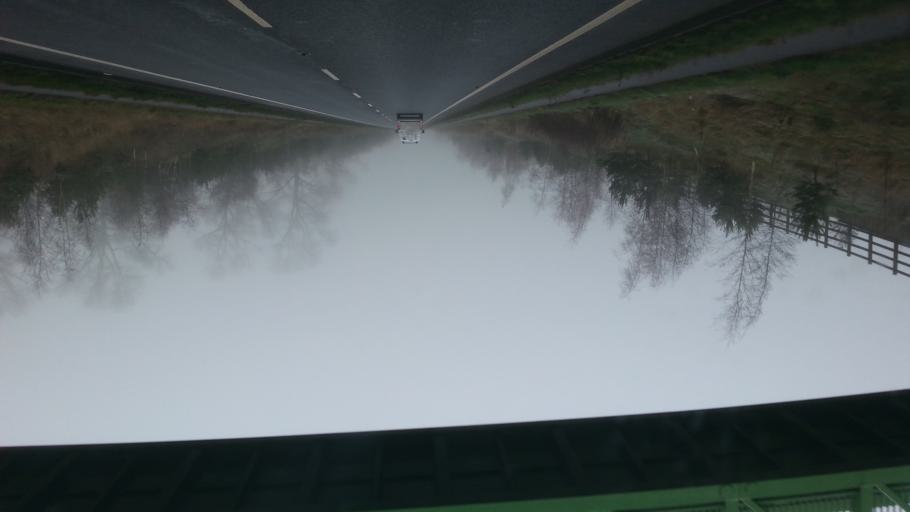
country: GB
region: England
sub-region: Cheshire East
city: Alderley Edge
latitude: 53.2788
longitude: -2.2437
